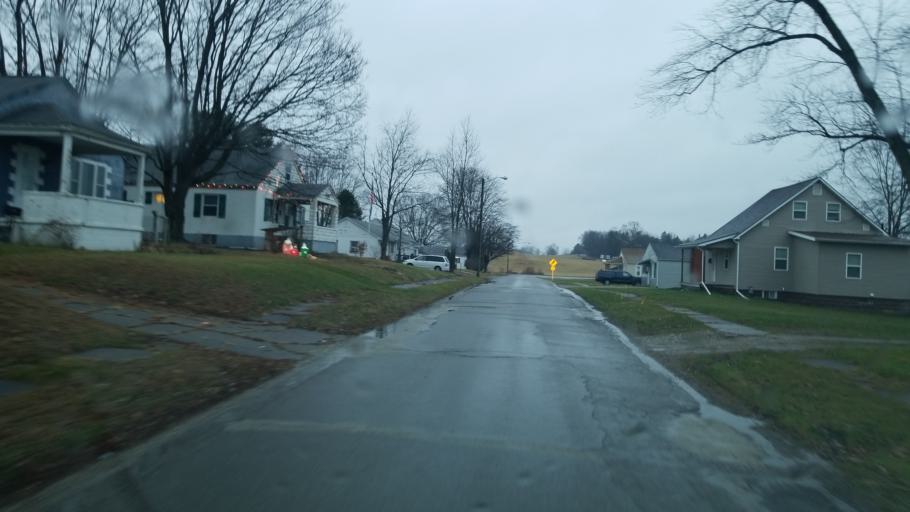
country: US
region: Ohio
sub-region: Licking County
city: Newark
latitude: 40.0728
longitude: -82.3804
